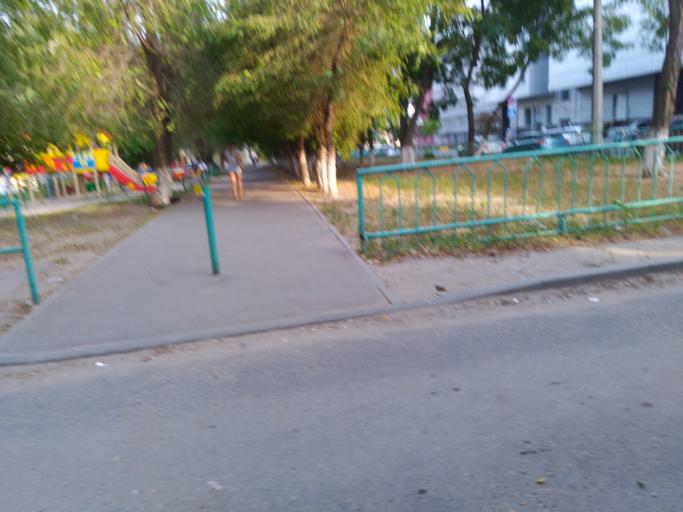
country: RU
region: Volgograd
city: Volgograd
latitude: 48.6977
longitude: 44.5026
